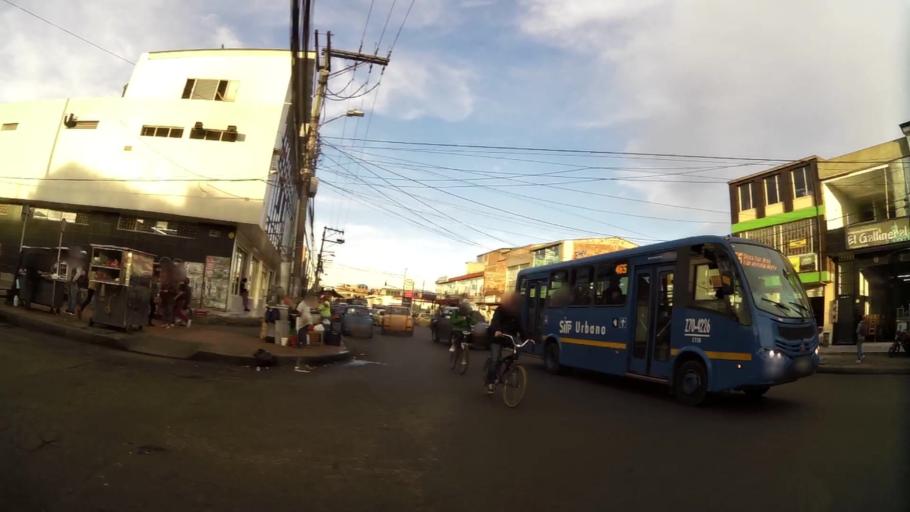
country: CO
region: Cundinamarca
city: Soacha
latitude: 4.6196
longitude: -74.1617
